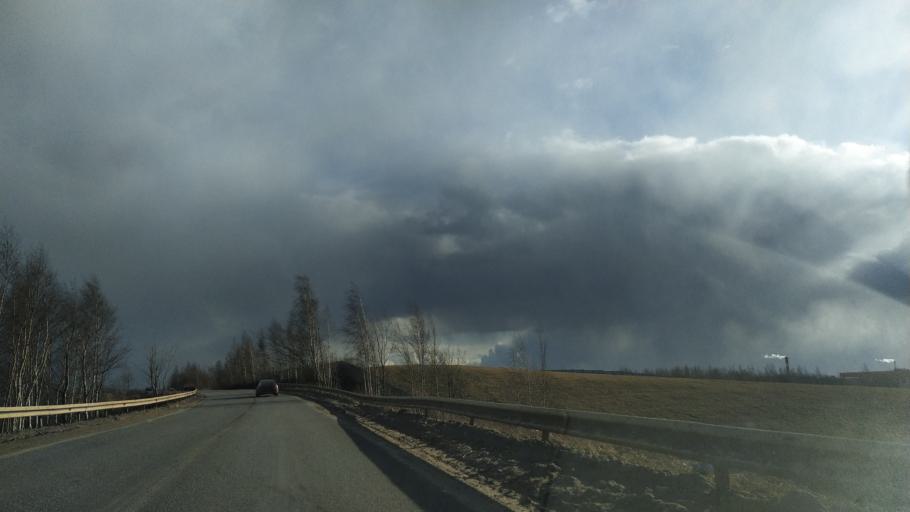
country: RU
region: Leningrad
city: Bugry
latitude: 60.0965
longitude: 30.3901
